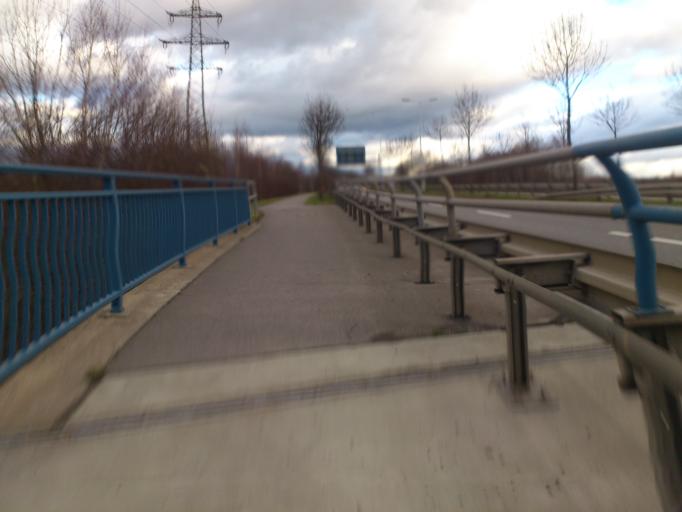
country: DE
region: Saxony
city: Chemnitz
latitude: 50.8001
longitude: 12.9187
